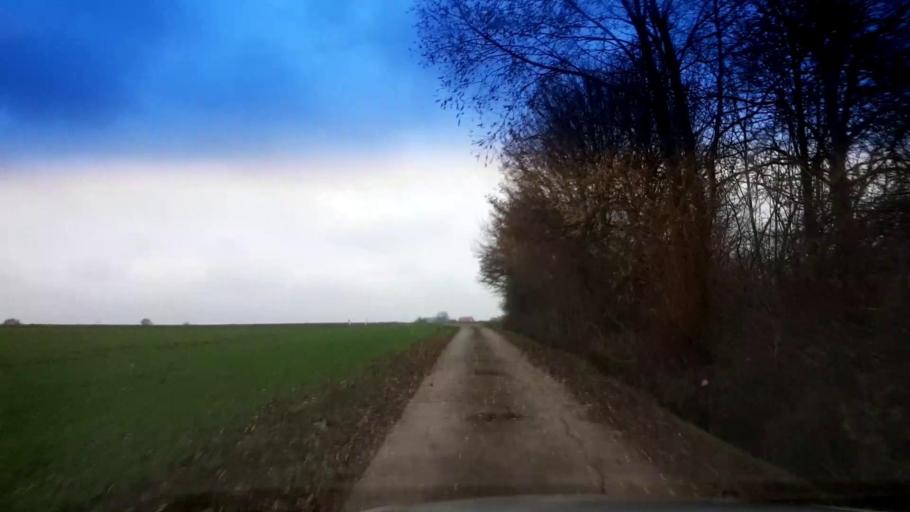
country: DE
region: Bavaria
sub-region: Upper Franconia
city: Zapfendorf
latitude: 49.9824
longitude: 10.9528
